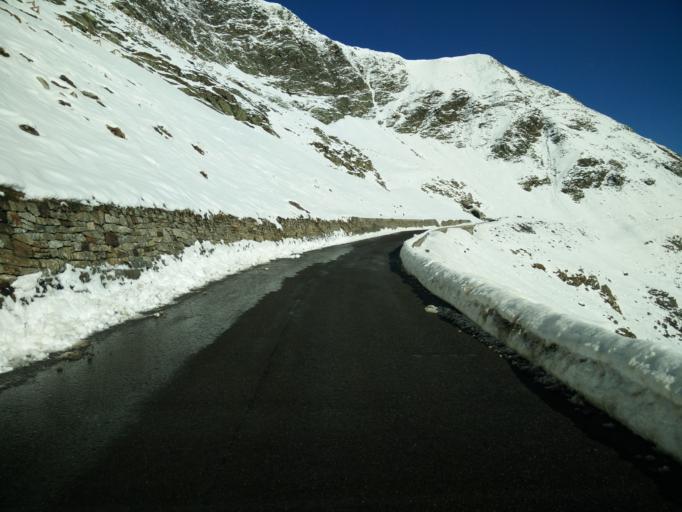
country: IT
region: Trentino-Alto Adige
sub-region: Bolzano
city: Moso in Passiria
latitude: 46.8877
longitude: 11.1101
